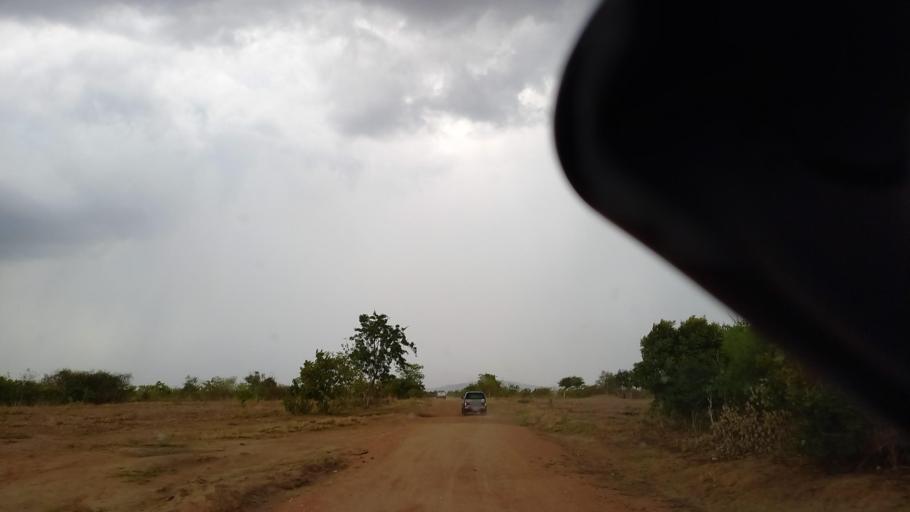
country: ZM
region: Lusaka
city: Kafue
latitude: -15.8680
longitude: 28.1922
